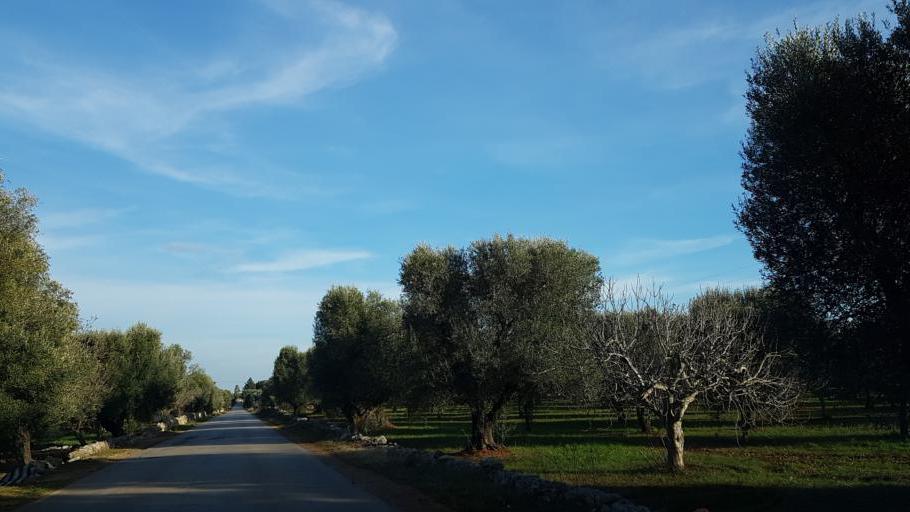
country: IT
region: Apulia
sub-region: Provincia di Brindisi
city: San Vito dei Normanni
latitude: 40.7054
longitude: 17.7079
